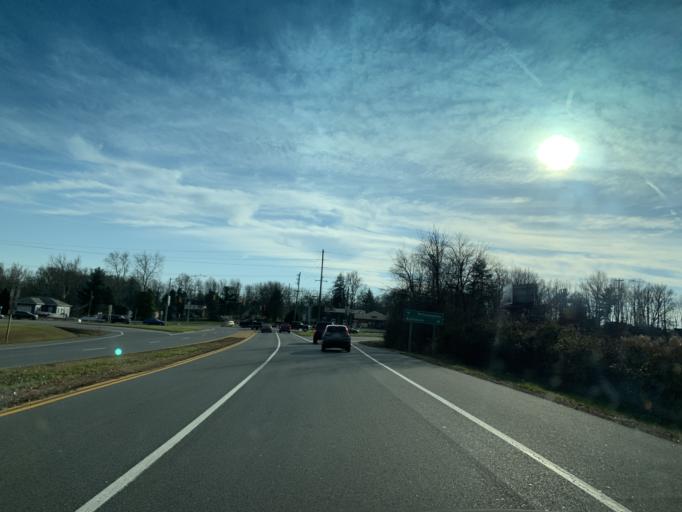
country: US
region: Maryland
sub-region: Cecil County
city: Elkton
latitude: 39.6081
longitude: -75.8537
